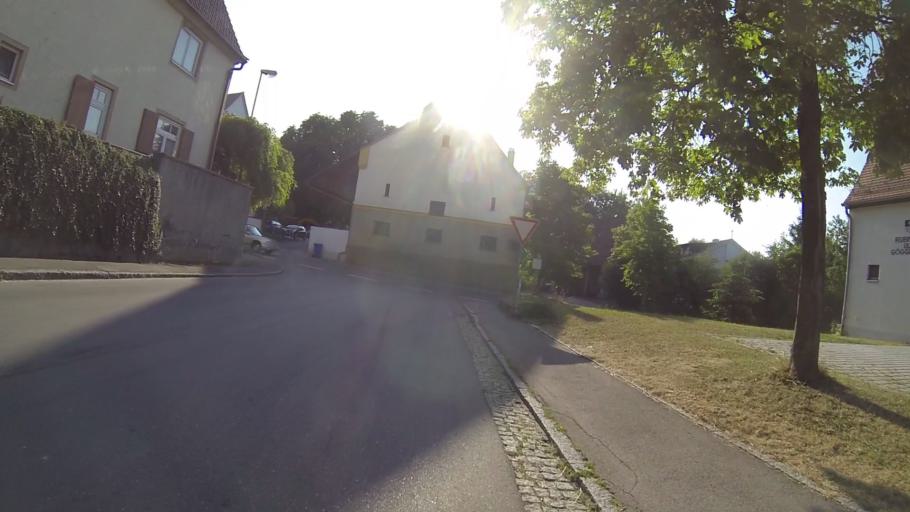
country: DE
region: Baden-Wuerttemberg
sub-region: Tuebingen Region
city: Erbach
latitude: 48.3413
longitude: 9.9410
